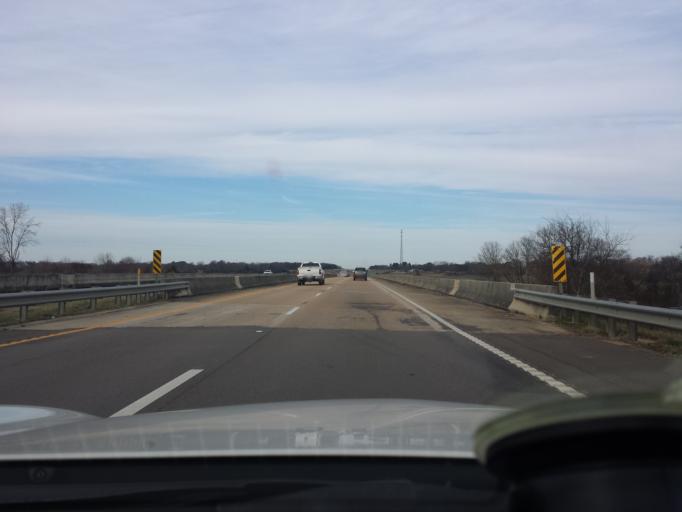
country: US
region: Mississippi
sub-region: Lee County
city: Shannon
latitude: 34.1015
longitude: -88.7007
